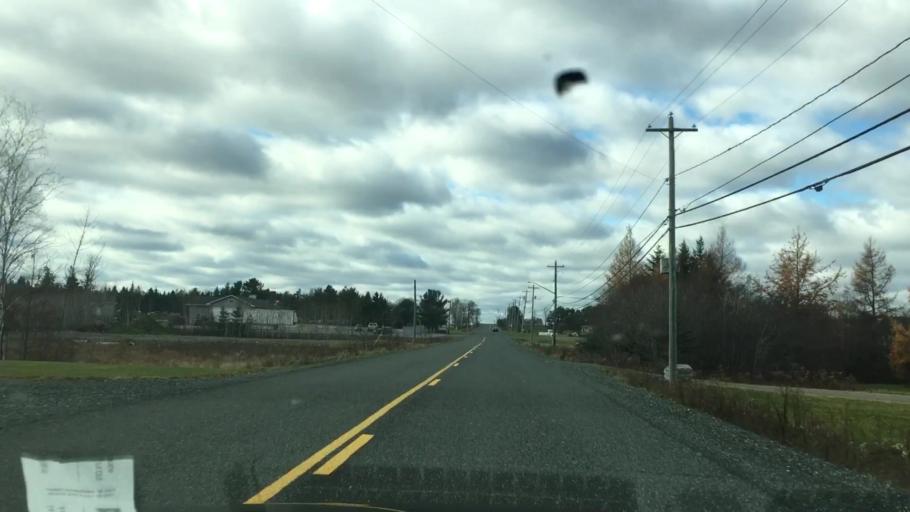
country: CA
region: New Brunswick
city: Florenceville-Bristol
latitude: 46.2889
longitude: -67.5408
